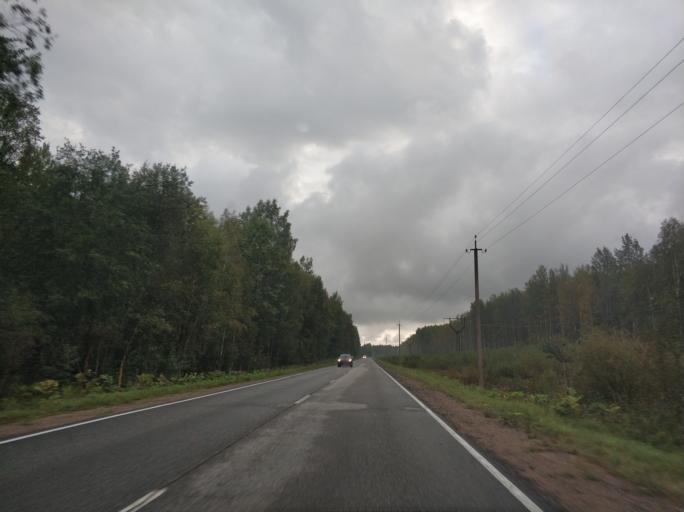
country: RU
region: Leningrad
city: Borisova Griva
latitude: 60.1077
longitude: 30.9598
